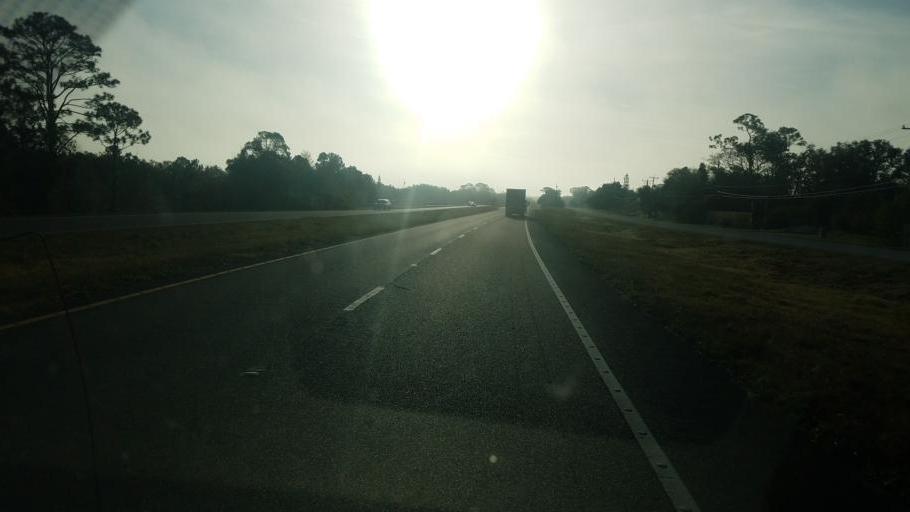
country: US
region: Florida
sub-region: Osceola County
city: Saint Cloud
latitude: 28.2398
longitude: -81.1987
